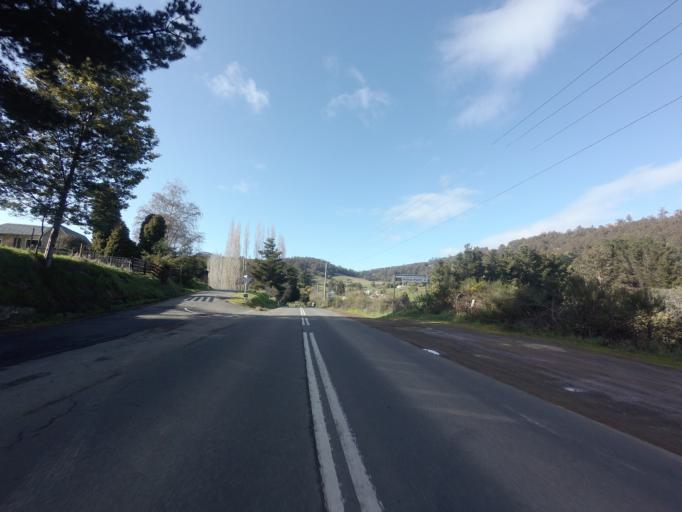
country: AU
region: Tasmania
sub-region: Huon Valley
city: Geeveston
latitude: -43.2372
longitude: 146.9908
